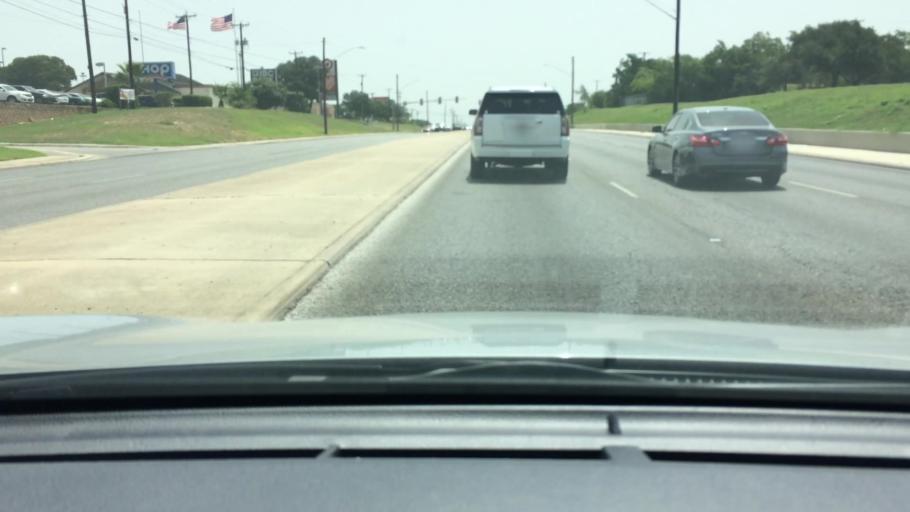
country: US
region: Texas
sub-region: Bexar County
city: San Antonio
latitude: 29.3517
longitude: -98.4423
